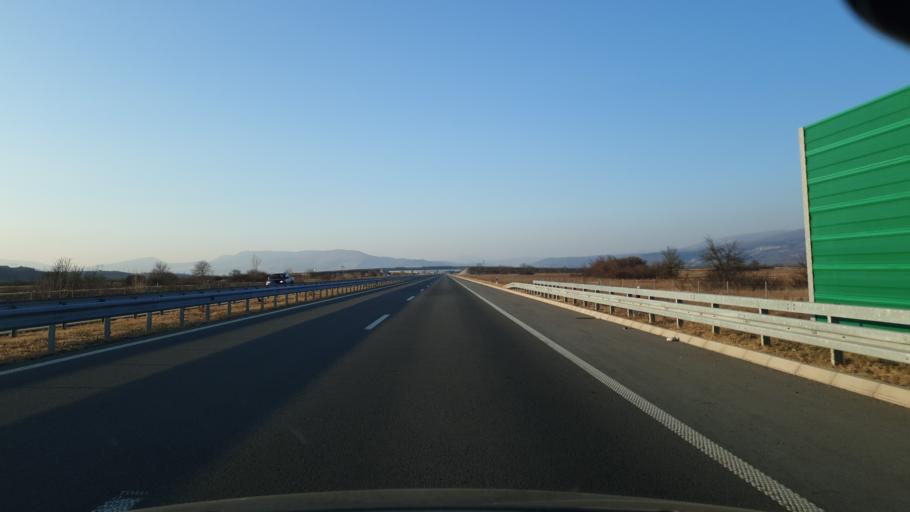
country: RS
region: Central Serbia
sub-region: Pirotski Okrug
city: Pirot
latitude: 43.1021
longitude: 22.6413
